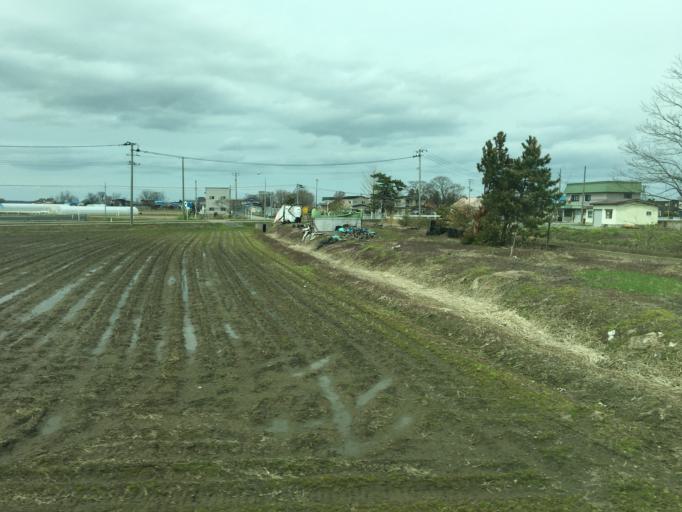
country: JP
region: Aomori
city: Shimokizukuri
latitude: 40.7862
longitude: 140.3624
